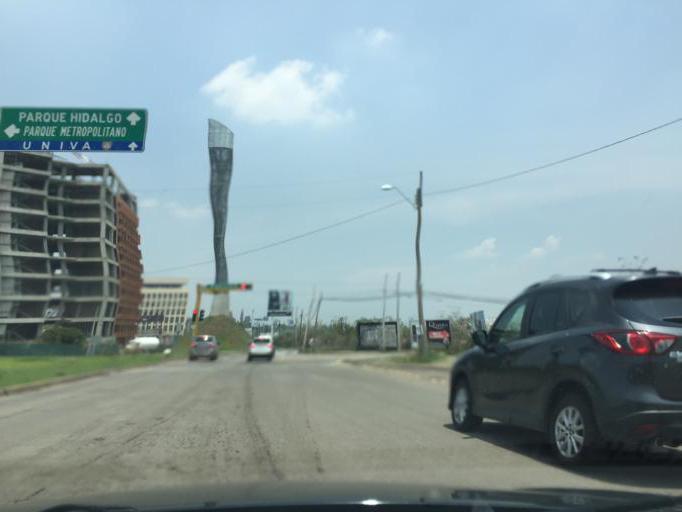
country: MX
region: Guanajuato
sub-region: Leon
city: La Ermita
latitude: 21.1729
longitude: -101.7355
